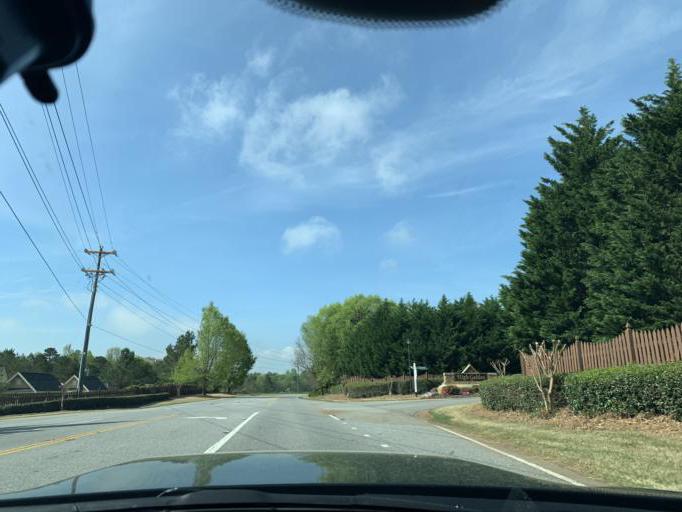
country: US
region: Georgia
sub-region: Forsyth County
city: Cumming
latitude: 34.2511
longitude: -84.0743
